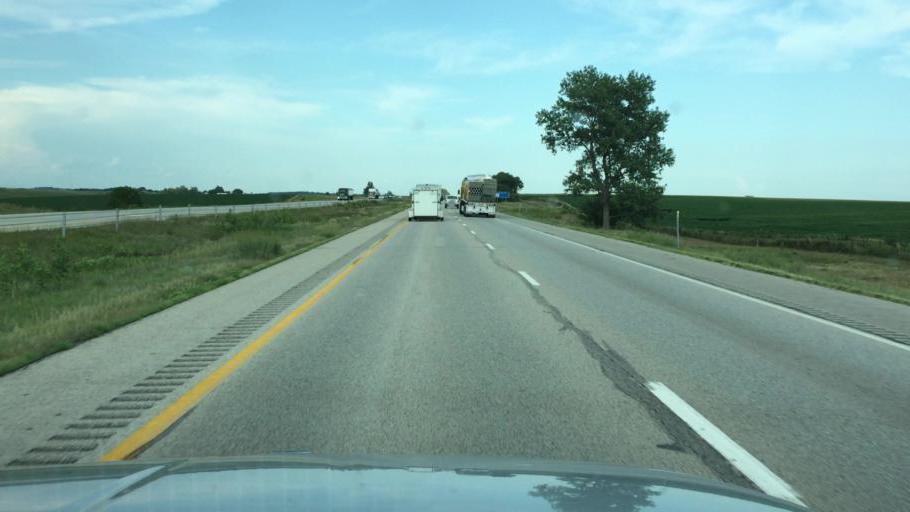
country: US
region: Iowa
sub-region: Johnson County
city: Tiffin
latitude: 41.6925
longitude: -91.7516
